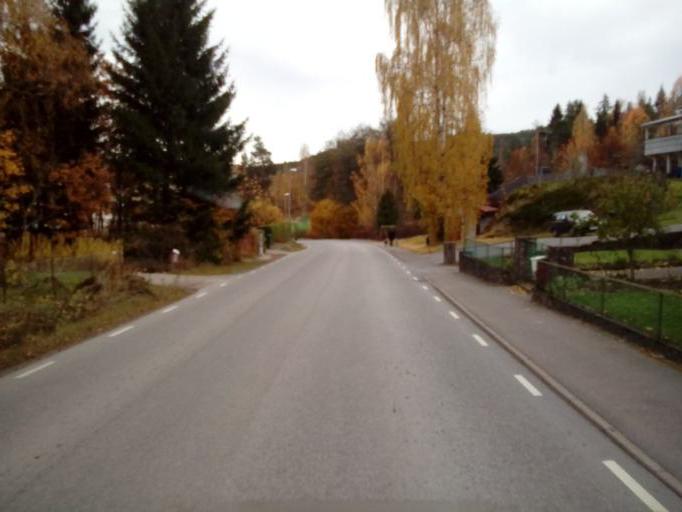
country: SE
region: OEstergoetland
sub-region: Kinda Kommun
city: Kisa
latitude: 57.9864
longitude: 15.6459
